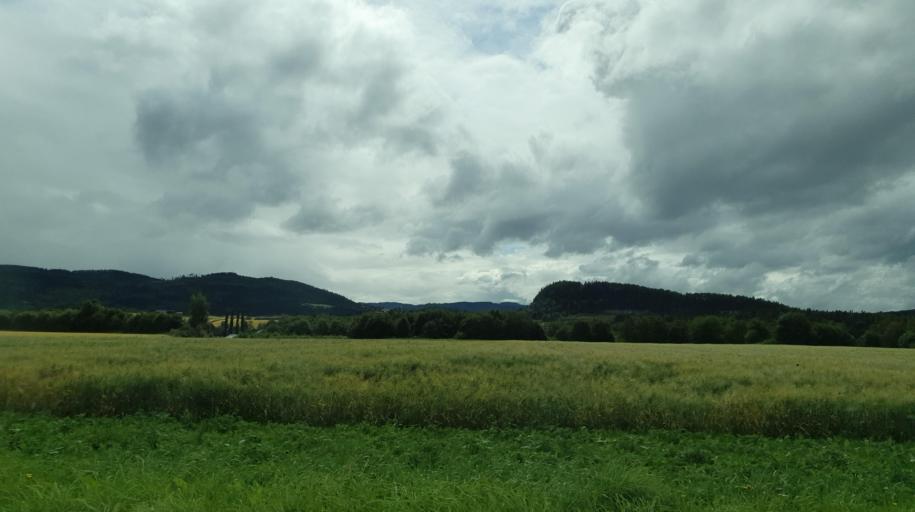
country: NO
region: Nord-Trondelag
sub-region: Stjordal
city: Stjordalshalsen
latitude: 63.4530
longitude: 10.9649
